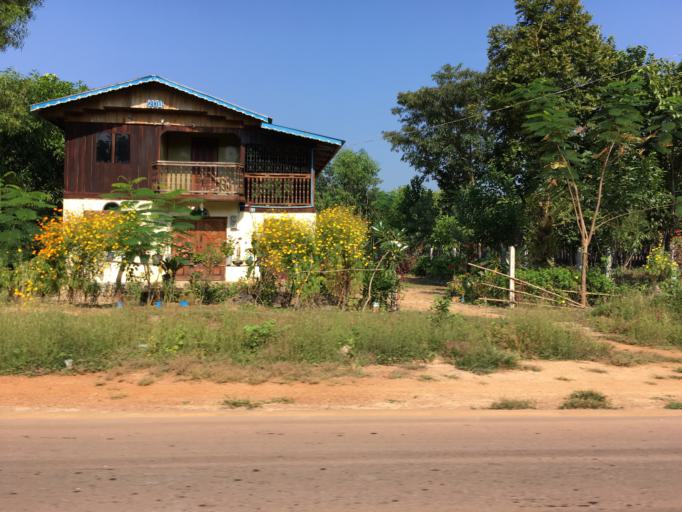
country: MM
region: Mon
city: Martaban
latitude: 16.6933
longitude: 97.7466
